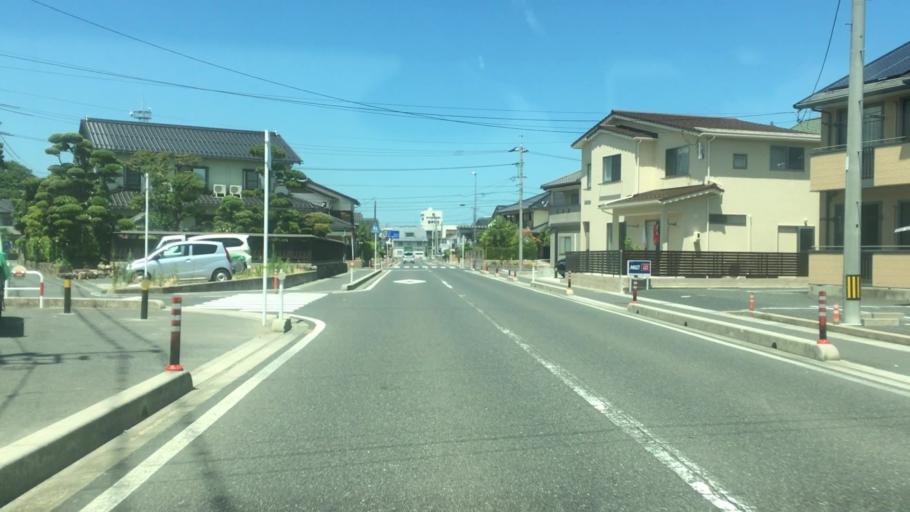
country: JP
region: Tottori
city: Tottori
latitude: 35.4855
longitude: 134.2238
